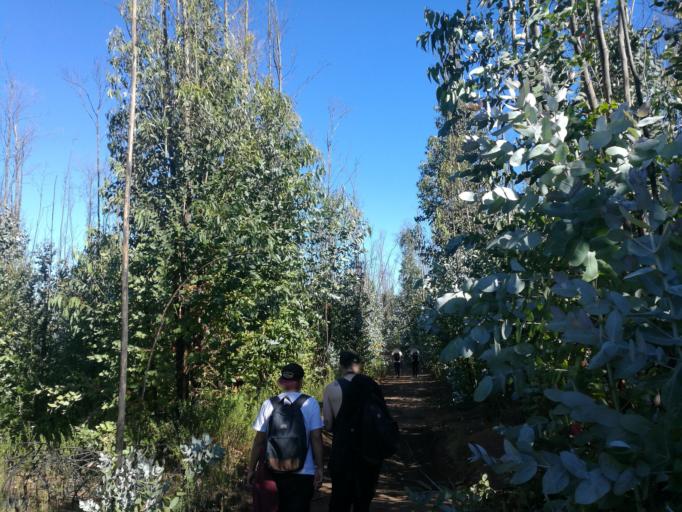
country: CL
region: Valparaiso
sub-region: Provincia de Valparaiso
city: Valparaiso
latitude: -33.0721
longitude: -71.6461
